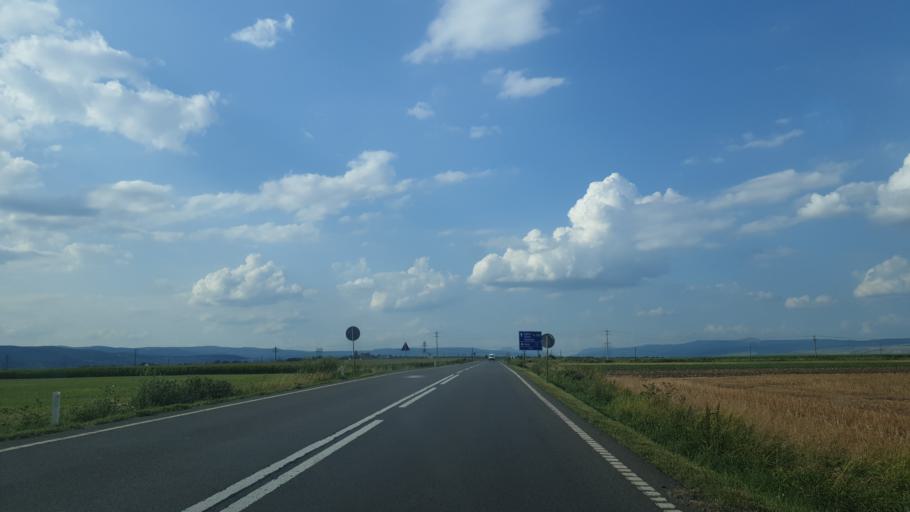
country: RO
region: Covasna
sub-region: Comuna Chichis
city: Chichis
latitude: 45.7954
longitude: 25.8043
